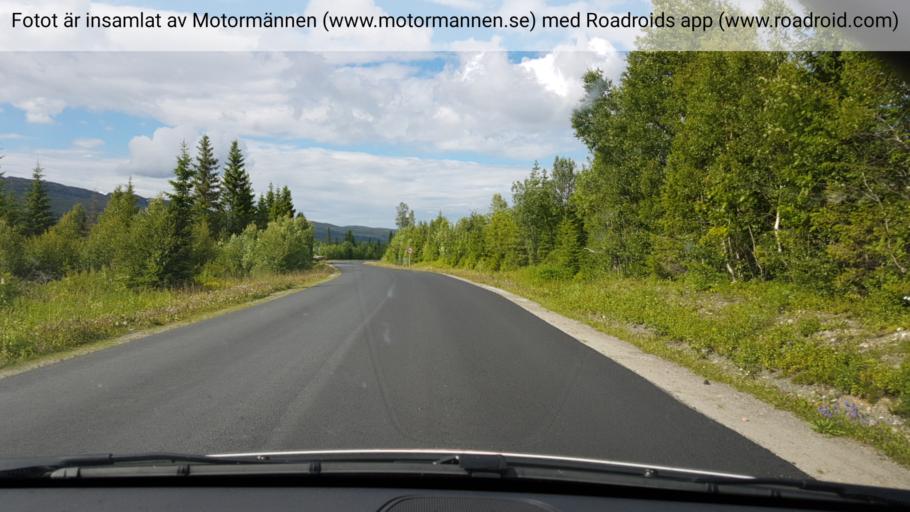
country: NO
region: Nord-Trondelag
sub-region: Meraker
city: Meraker
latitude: 63.6551
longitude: 12.2478
